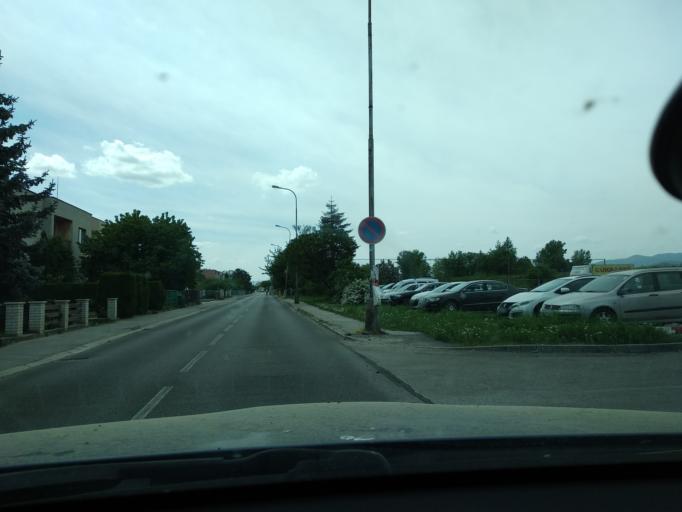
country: SK
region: Trenciansky
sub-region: Okres Trencin
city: Trencin
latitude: 48.8835
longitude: 18.0222
